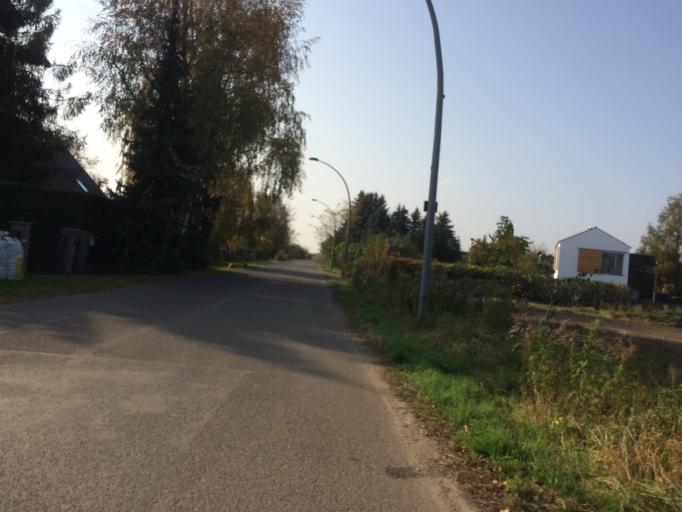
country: DE
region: Berlin
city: Stadtrandsiedlung Malchow
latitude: 52.5938
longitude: 13.4708
